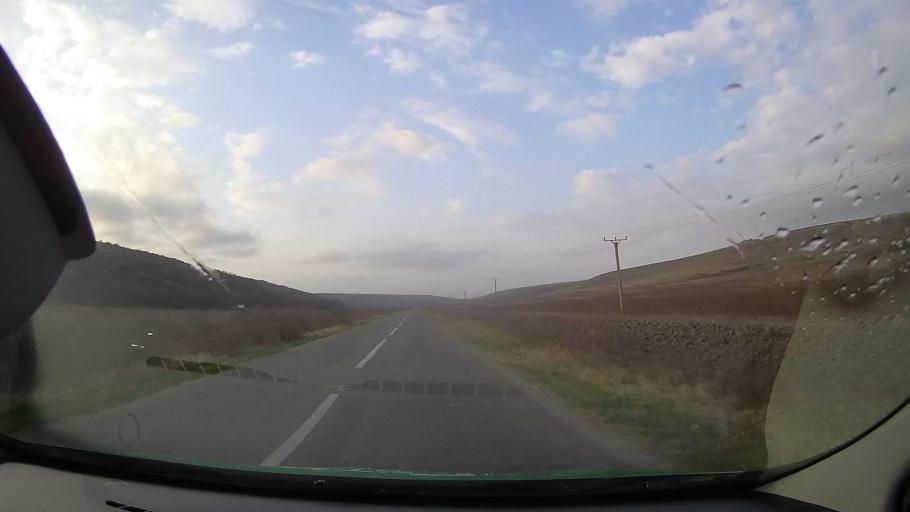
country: RO
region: Constanta
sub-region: Comuna Dobromir
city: Dobromir
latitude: 44.0265
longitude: 27.8655
